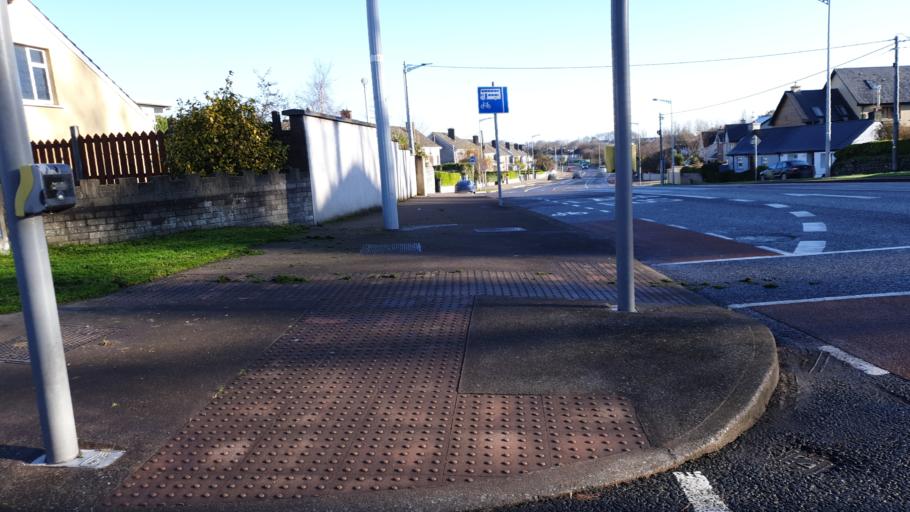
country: IE
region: Munster
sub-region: County Cork
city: Cork
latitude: 51.8869
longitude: -8.4285
